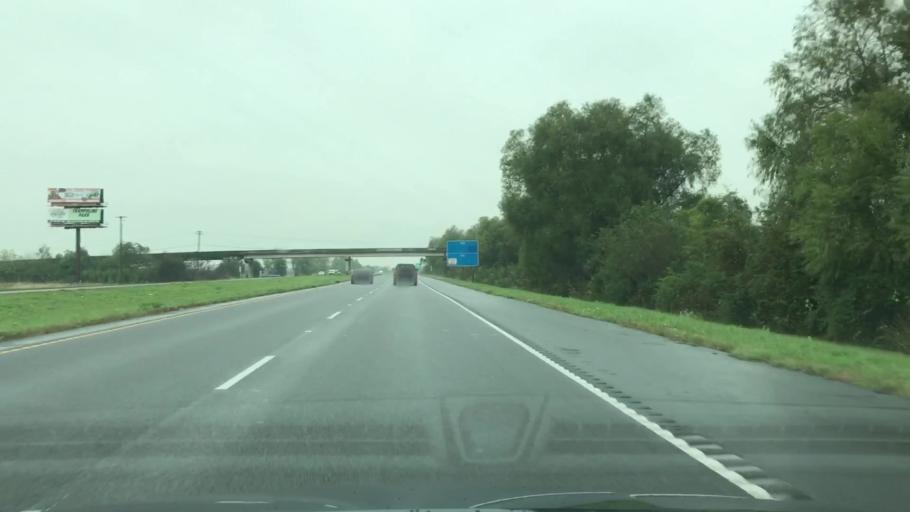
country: US
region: Louisiana
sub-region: Lafourche Parish
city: Raceland
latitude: 29.6898
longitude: -90.6196
